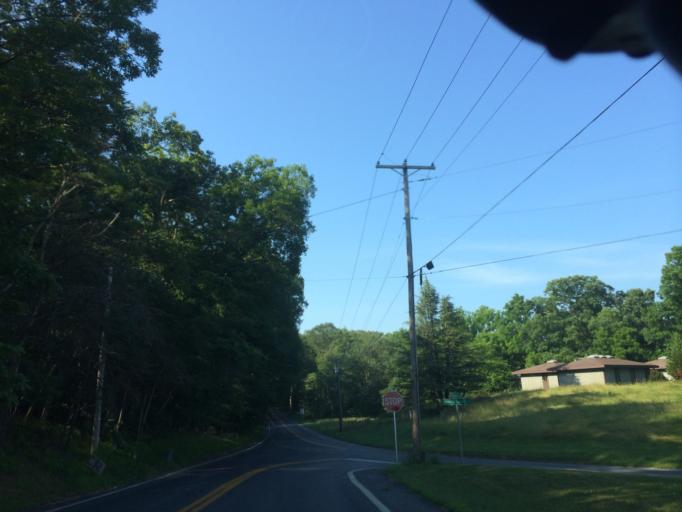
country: US
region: Maryland
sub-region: Montgomery County
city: Olney
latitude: 39.2691
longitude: -77.0721
